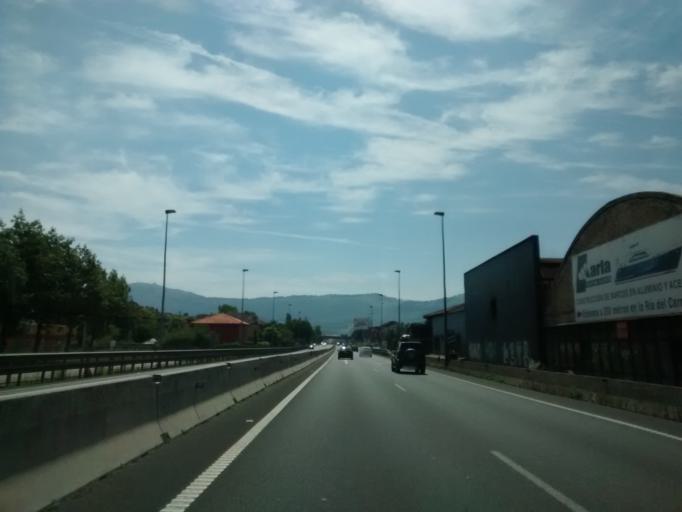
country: ES
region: Cantabria
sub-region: Provincia de Cantabria
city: El Astillero
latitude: 43.4156
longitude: -3.8391
